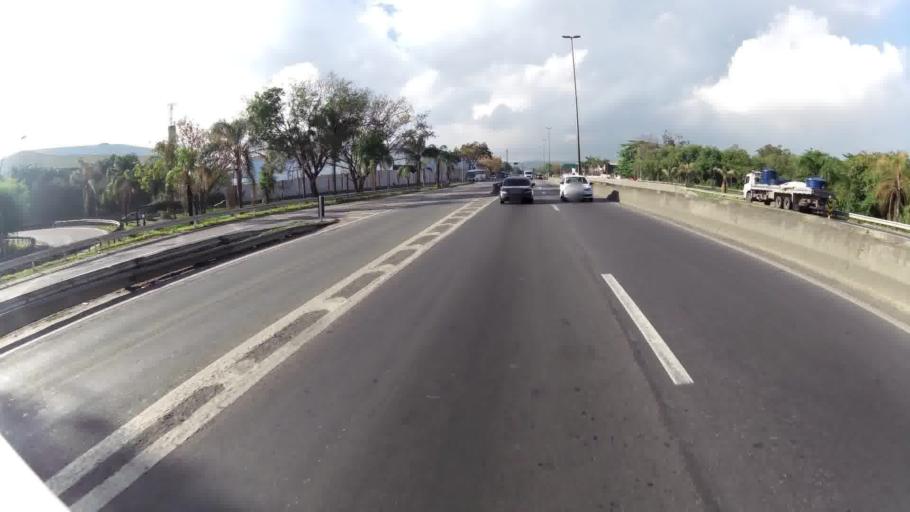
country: BR
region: Rio de Janeiro
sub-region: Duque De Caxias
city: Duque de Caxias
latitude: -22.8088
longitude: -43.2888
